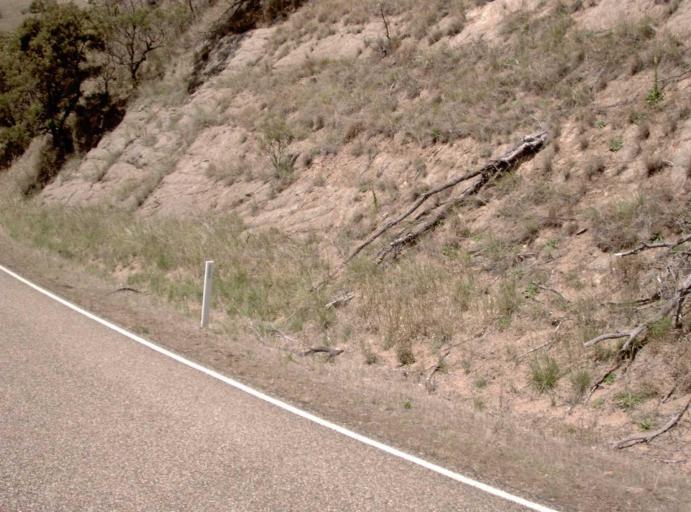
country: AU
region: Victoria
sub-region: Alpine
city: Mount Beauty
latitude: -37.1640
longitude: 147.6663
